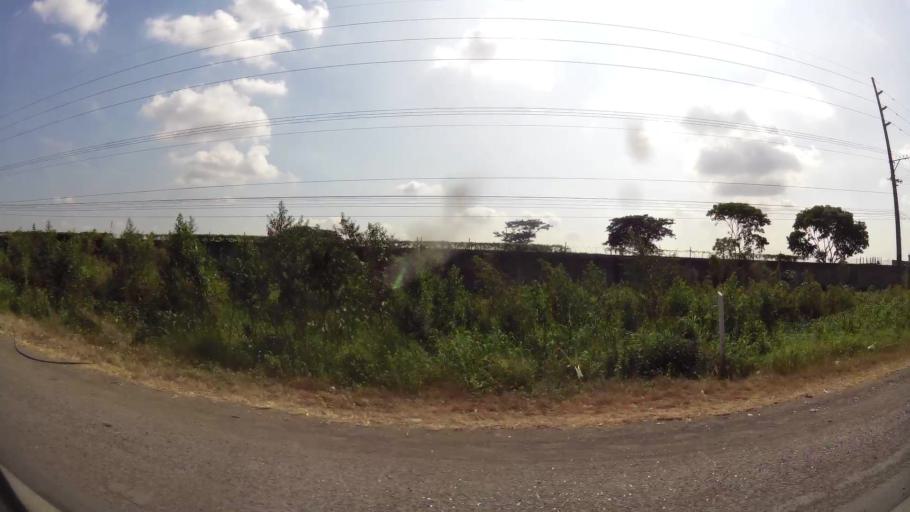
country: EC
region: Guayas
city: Eloy Alfaro
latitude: -2.1817
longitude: -79.8202
